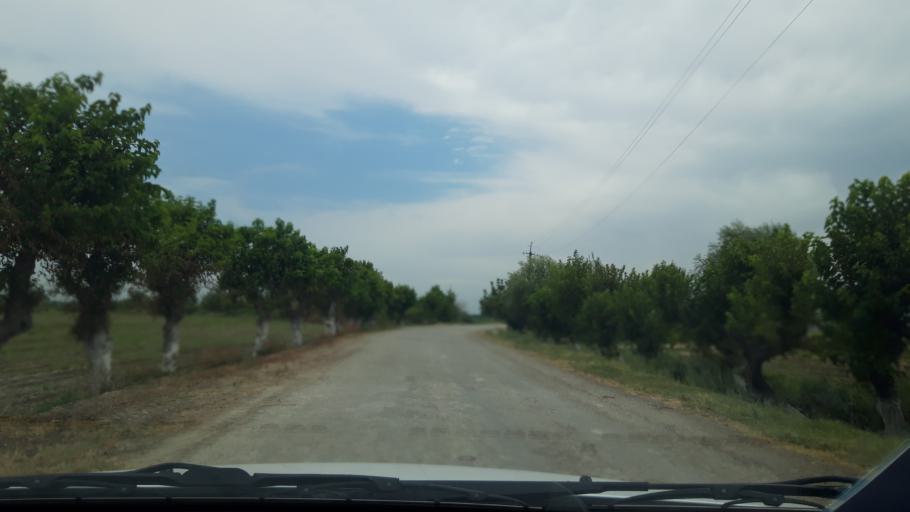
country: UZ
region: Namangan
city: Uychi
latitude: 41.0192
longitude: 71.9221
